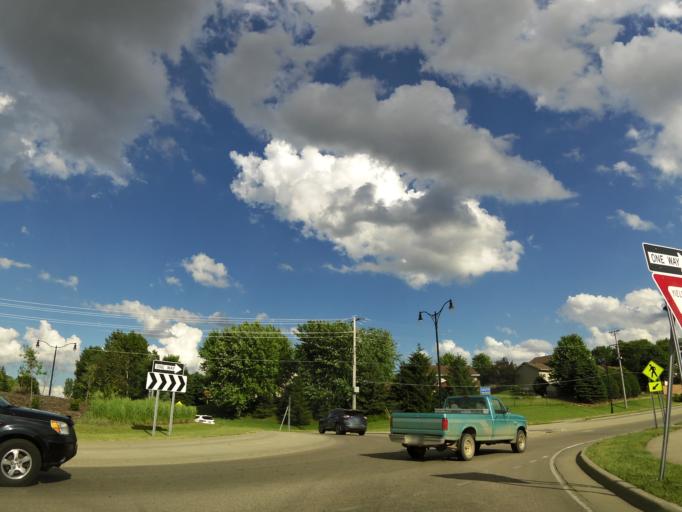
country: US
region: Minnesota
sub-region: Carver County
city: Waconia
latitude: 44.8364
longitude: -93.7889
